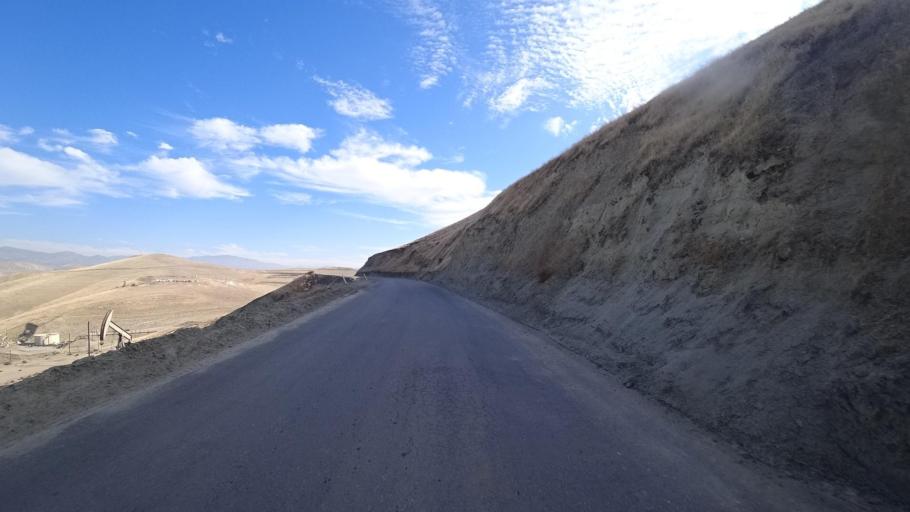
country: US
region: California
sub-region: Kern County
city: Oildale
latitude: 35.4885
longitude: -118.8889
